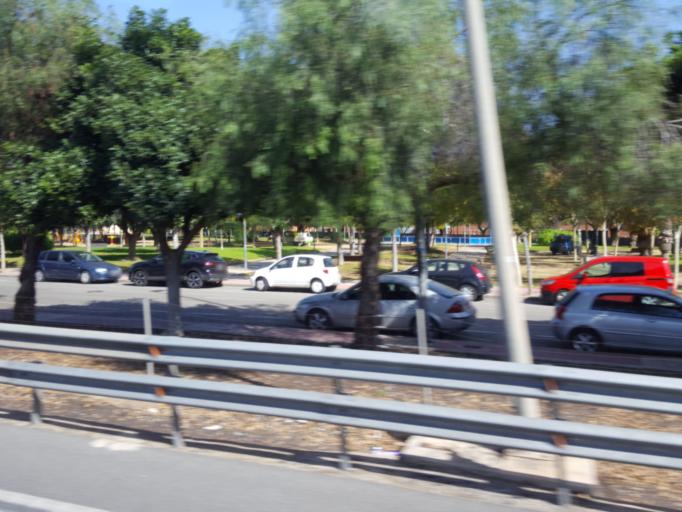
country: ES
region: Murcia
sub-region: Murcia
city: Murcia
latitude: 37.9959
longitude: -1.1494
